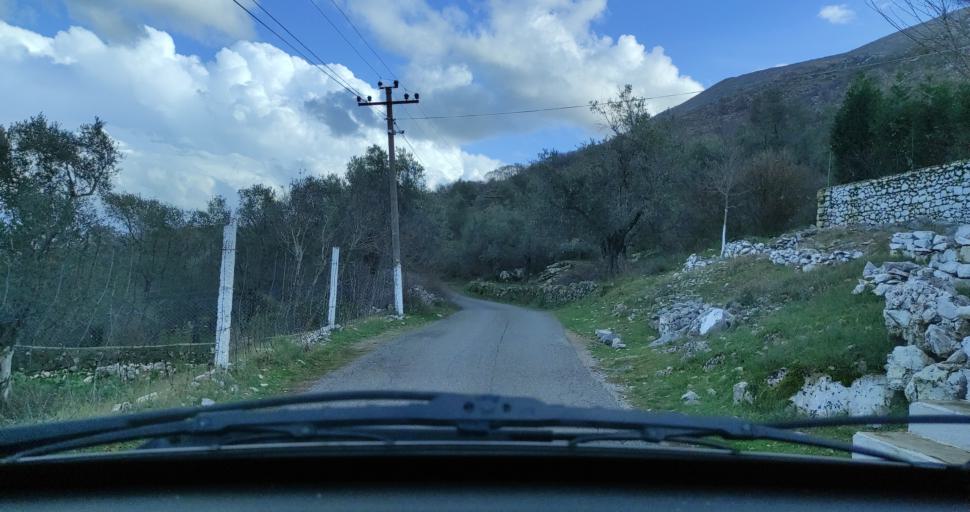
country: AL
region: Shkoder
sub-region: Rrethi i Shkodres
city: Dajc
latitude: 42.0704
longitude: 19.4035
